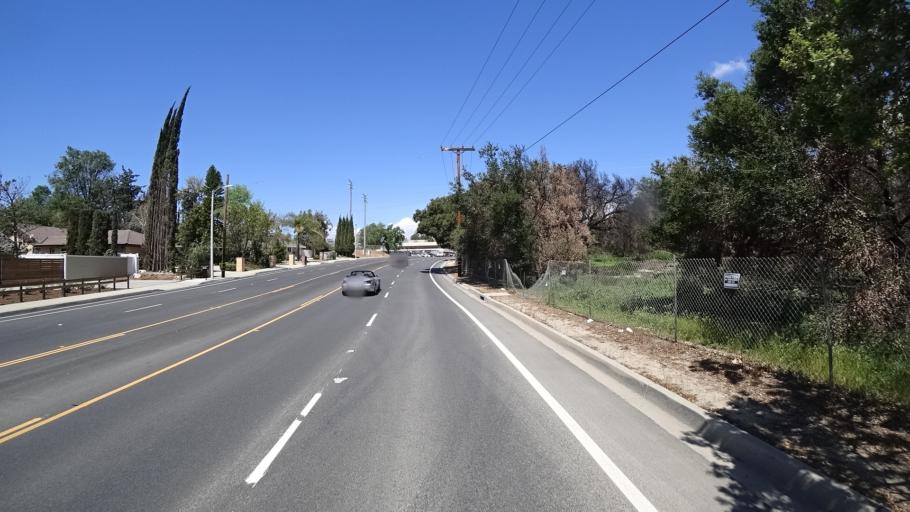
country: US
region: California
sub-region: Ventura County
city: Thousand Oaks
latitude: 34.2051
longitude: -118.8393
